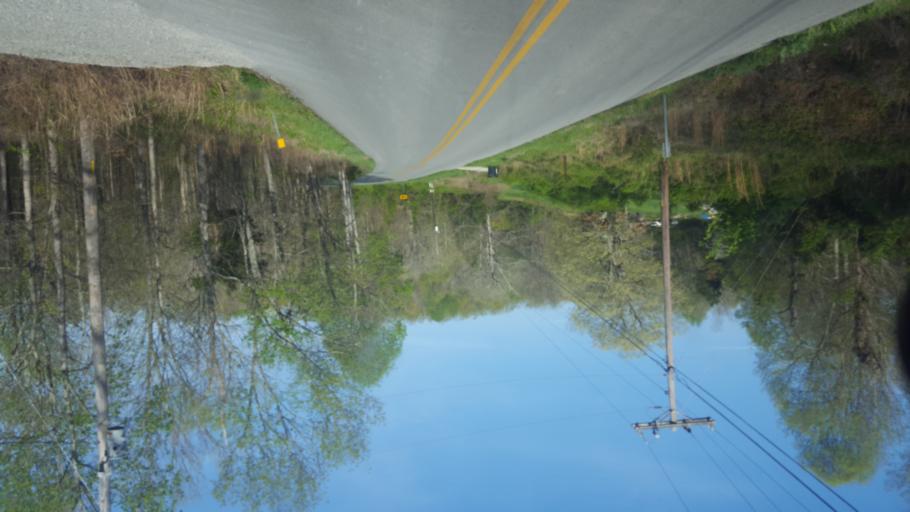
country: US
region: Kentucky
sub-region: Edmonson County
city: Brownsville
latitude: 37.3192
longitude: -86.1136
